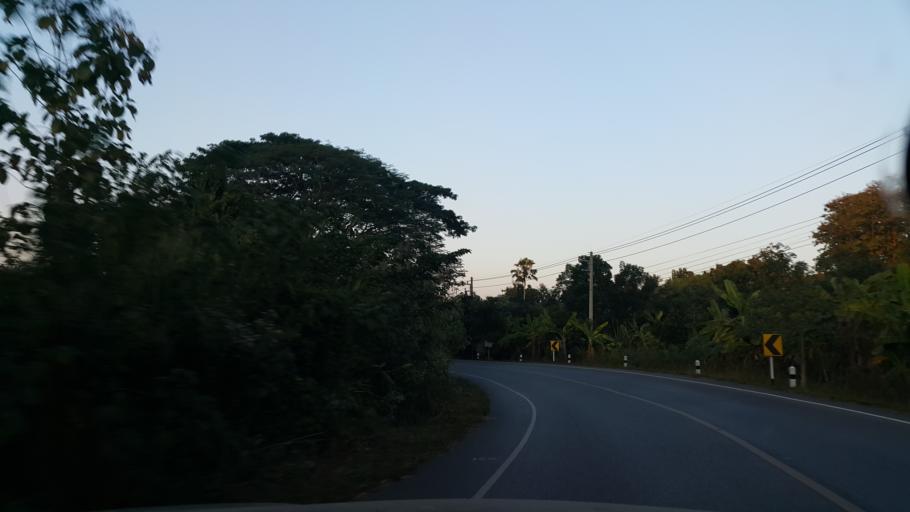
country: TH
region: Phrae
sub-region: Amphoe Wang Chin
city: Wang Chin
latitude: 17.8404
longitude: 99.6415
